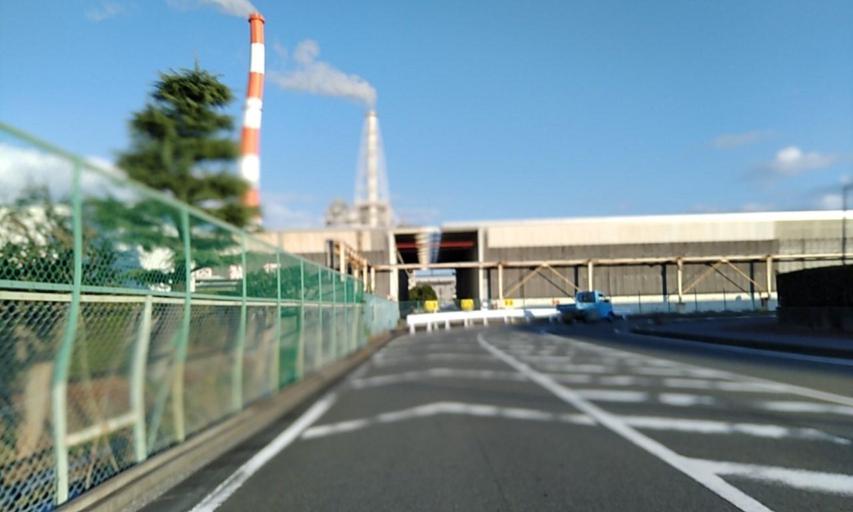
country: JP
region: Shizuoka
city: Fuji
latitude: 35.1457
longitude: 138.6670
